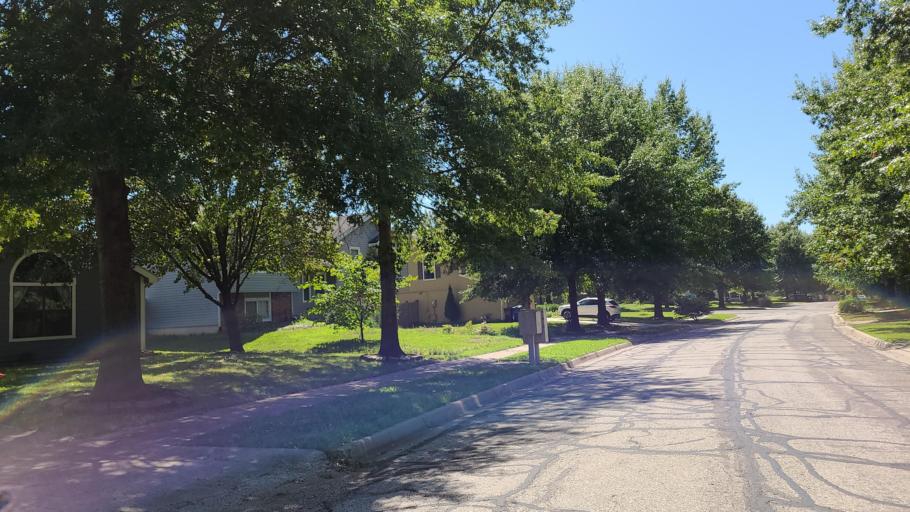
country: US
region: Kansas
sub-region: Douglas County
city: Lawrence
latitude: 38.9324
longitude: -95.2085
